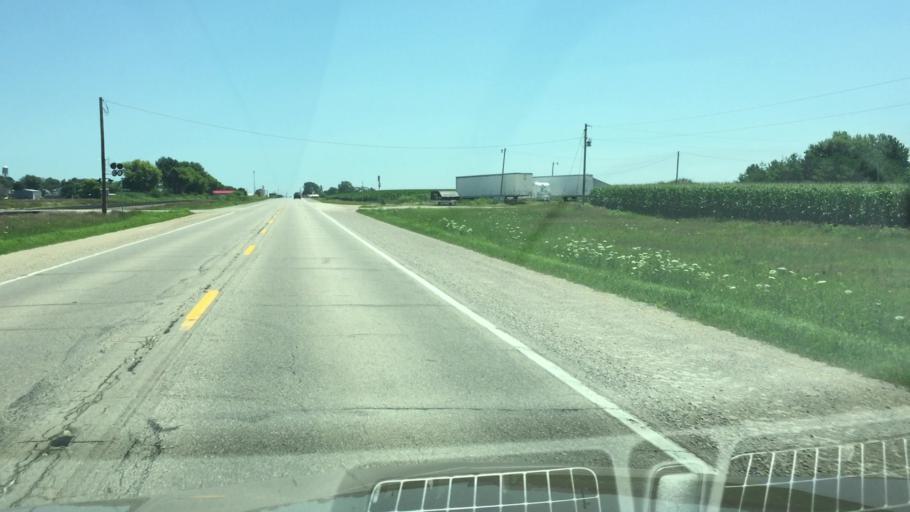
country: US
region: Iowa
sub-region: Cedar County
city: Mechanicsville
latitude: 41.9059
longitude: -91.2699
